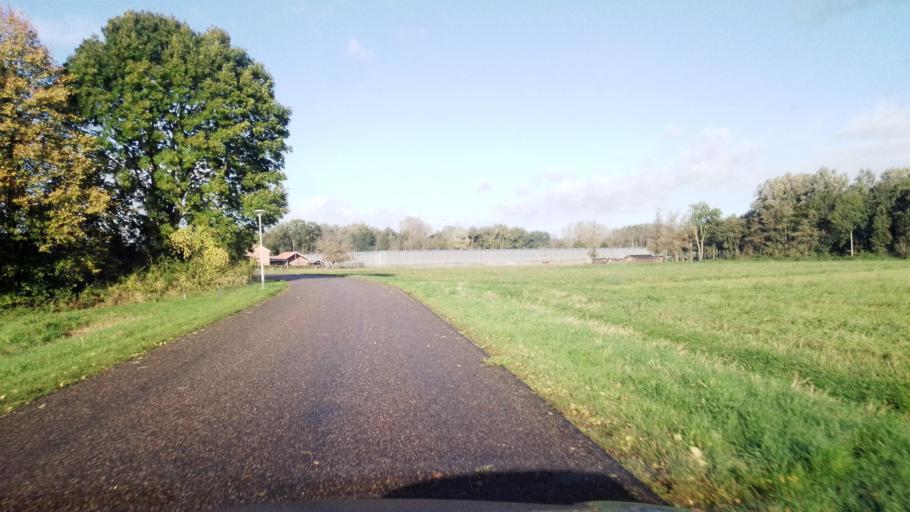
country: NL
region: Limburg
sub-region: Gemeente Venlo
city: Tegelen
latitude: 51.3574
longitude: 6.1063
